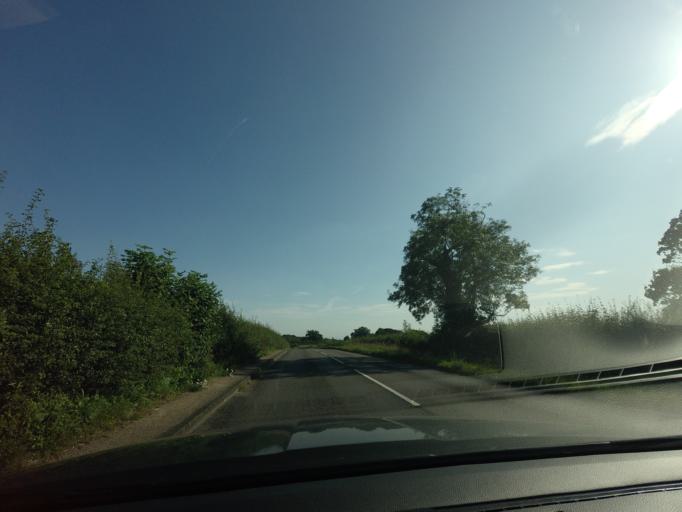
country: GB
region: England
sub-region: Nottinghamshire
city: Eastwood
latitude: 53.0417
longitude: -1.2972
